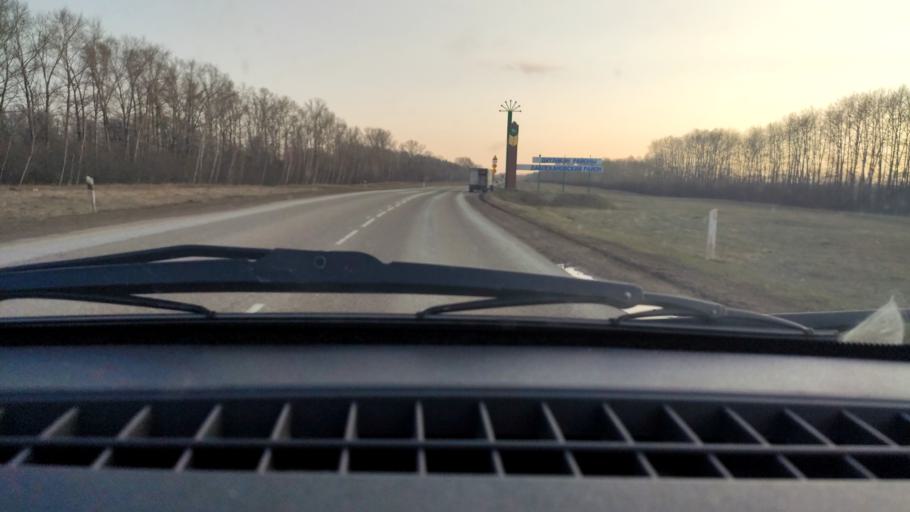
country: RU
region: Bashkortostan
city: Davlekanovo
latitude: 54.3621
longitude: 55.1953
